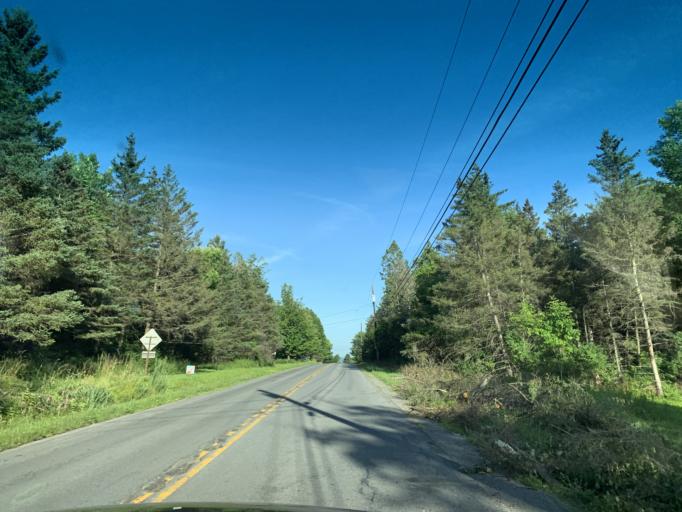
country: US
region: New York
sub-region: Oneida County
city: Clinton
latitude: 43.0547
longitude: -75.4299
